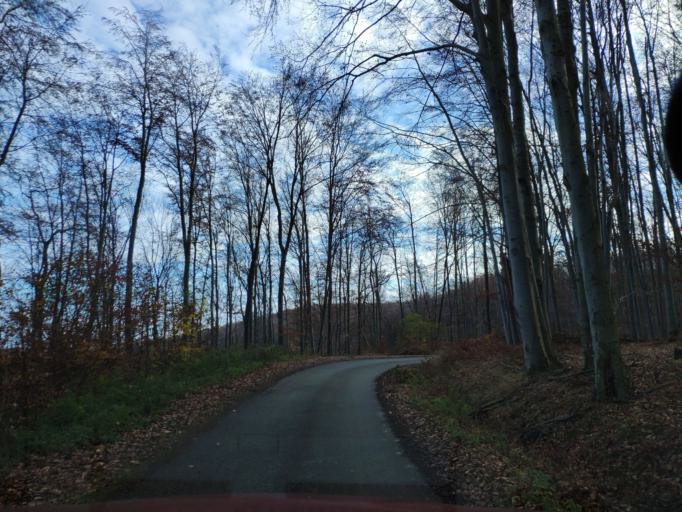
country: HU
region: Borsod-Abauj-Zemplen
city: Gonc
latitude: 48.5834
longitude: 21.4722
